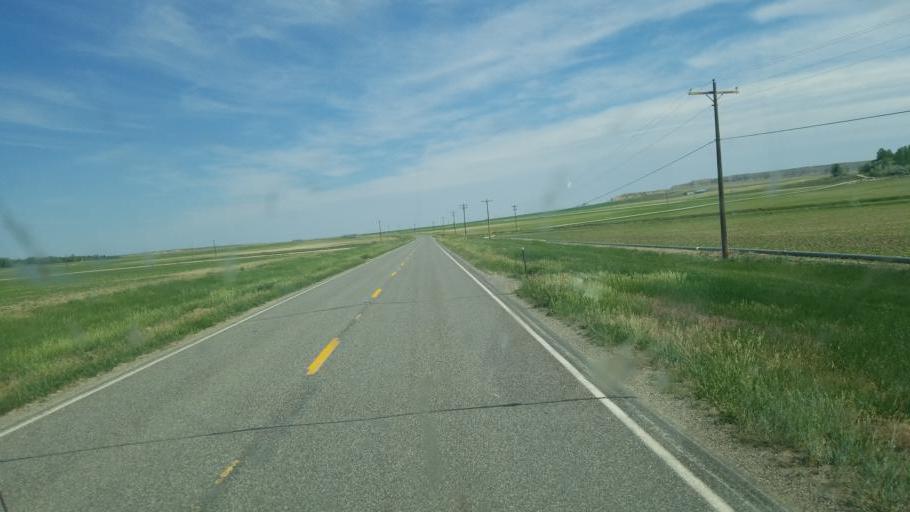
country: US
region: Wyoming
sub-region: Park County
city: Powell
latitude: 44.7657
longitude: -108.9313
